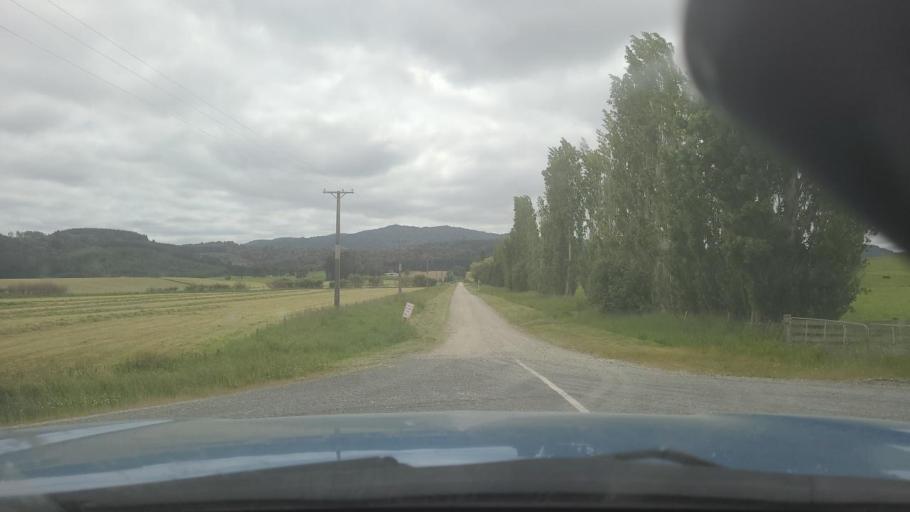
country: NZ
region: Southland
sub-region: Gore District
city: Gore
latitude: -46.1867
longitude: 168.6751
